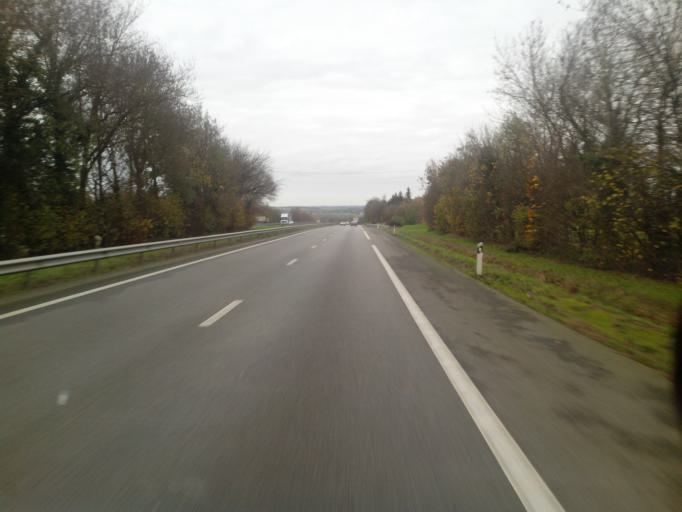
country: FR
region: Brittany
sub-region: Departement d'Ille-et-Vilaine
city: Grand-Fougeray
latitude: 47.7252
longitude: -1.7115
